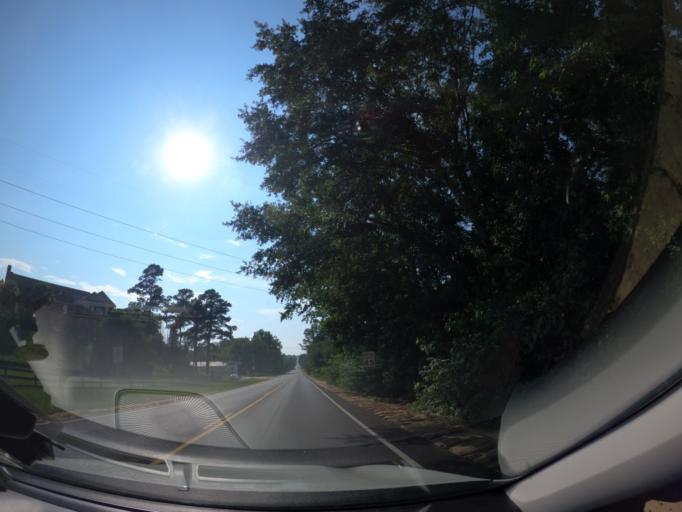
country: US
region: South Carolina
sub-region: Aiken County
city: Jackson
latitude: 33.4061
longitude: -81.7823
